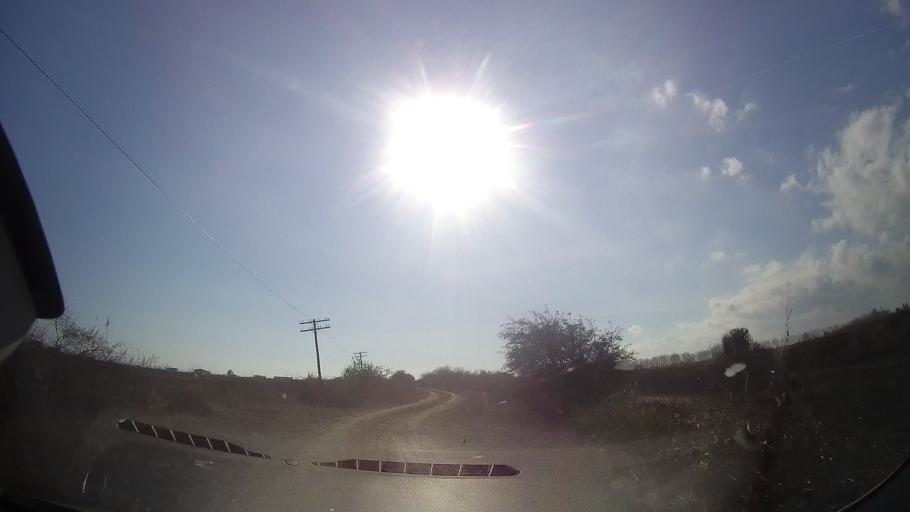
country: RO
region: Constanta
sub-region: Comuna Tuzla
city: Tuzla
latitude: 43.9760
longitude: 28.6441
